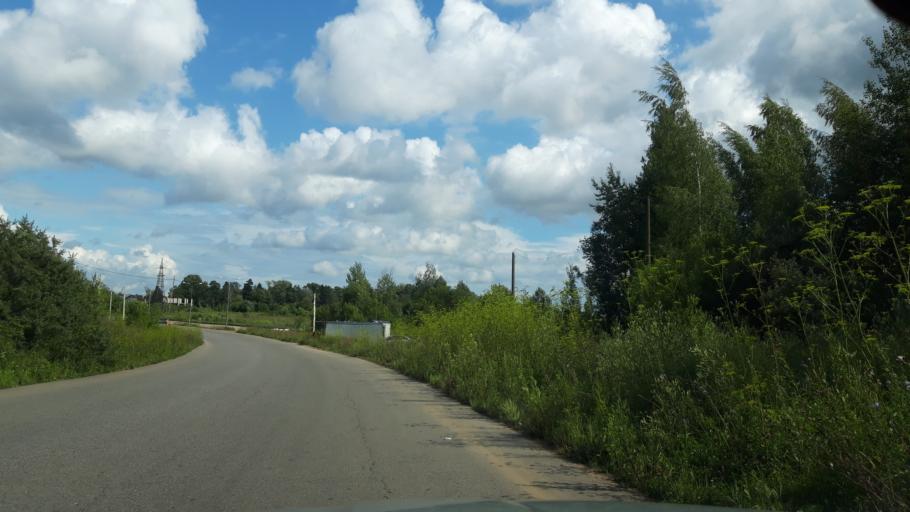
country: RU
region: Moscow
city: Zelenograd
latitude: 55.9641
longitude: 37.1726
